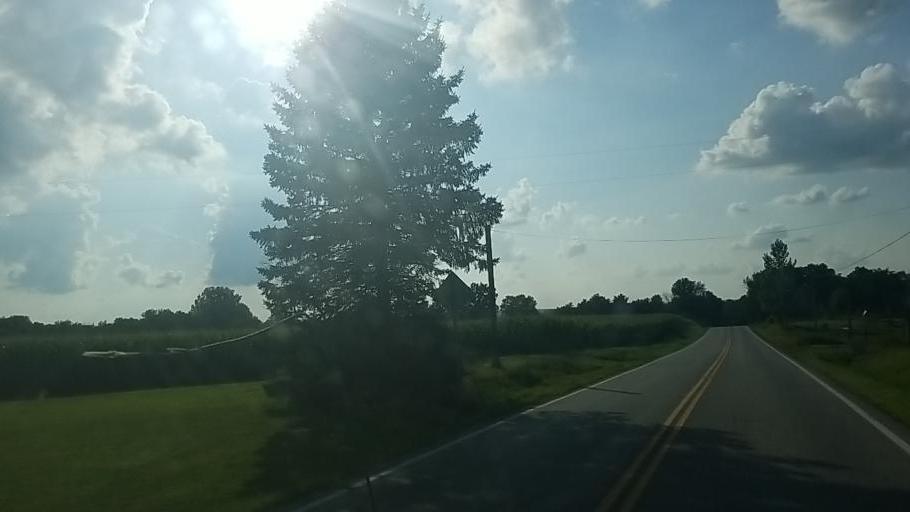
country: US
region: Ohio
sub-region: Wayne County
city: West Salem
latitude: 40.8832
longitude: -82.1164
